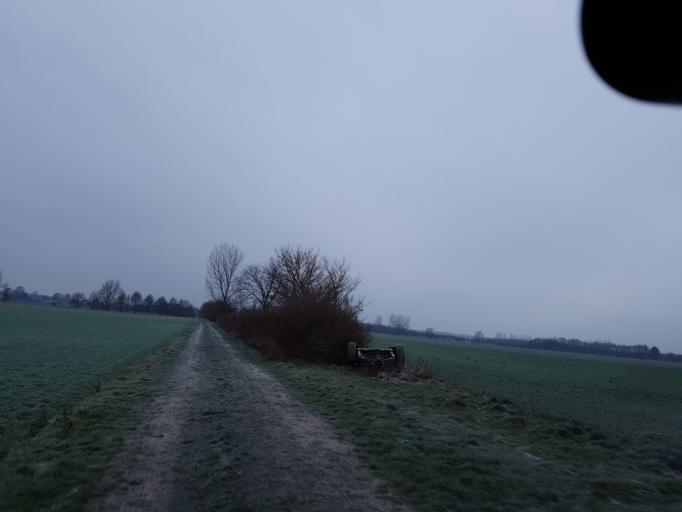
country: DE
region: Brandenburg
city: Ruckersdorf
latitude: 51.5722
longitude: 13.5520
